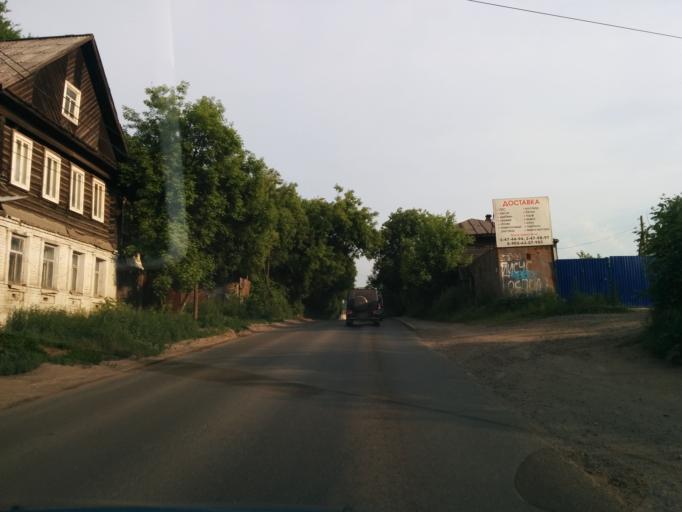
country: RU
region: Perm
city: Perm
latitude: 58.0411
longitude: 56.3180
